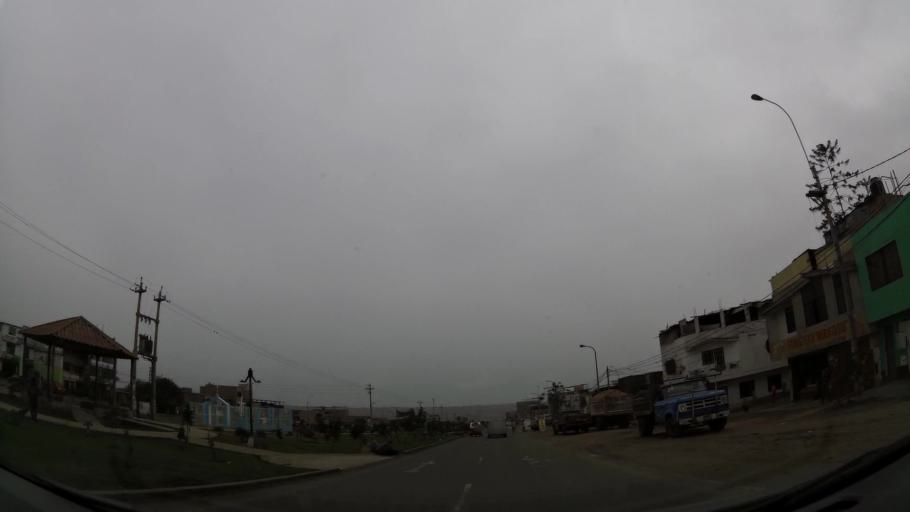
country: PE
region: Lima
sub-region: Lima
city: Surco
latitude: -12.2213
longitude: -76.9333
